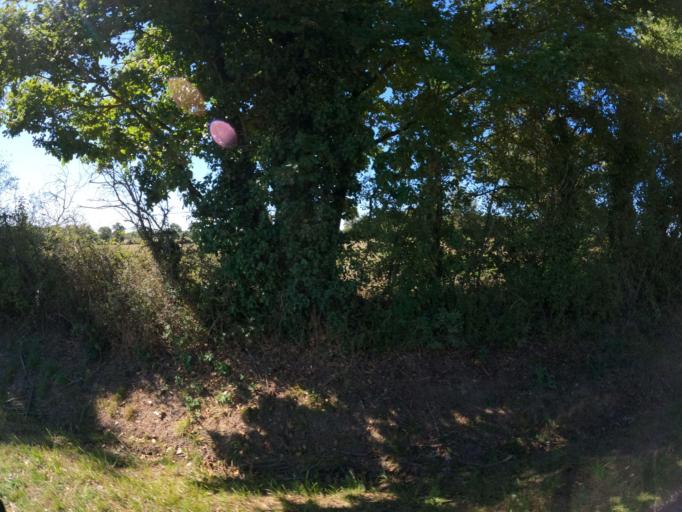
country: FR
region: Poitou-Charentes
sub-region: Departement de la Vienne
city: Lathus-Saint-Remy
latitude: 46.2812
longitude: 1.0122
